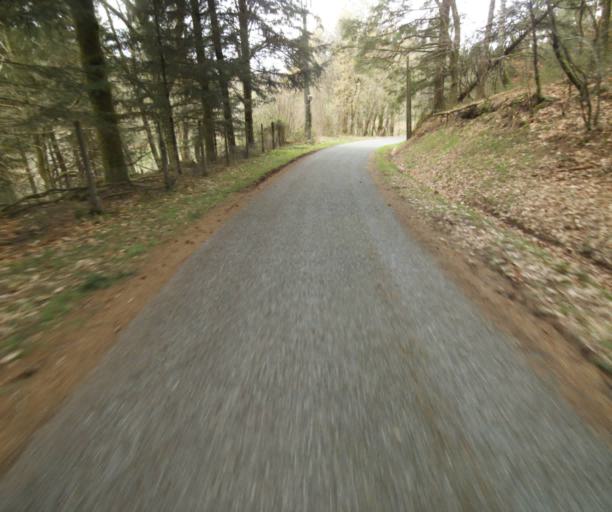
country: FR
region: Limousin
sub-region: Departement de la Correze
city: Correze
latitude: 45.2899
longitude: 1.9308
